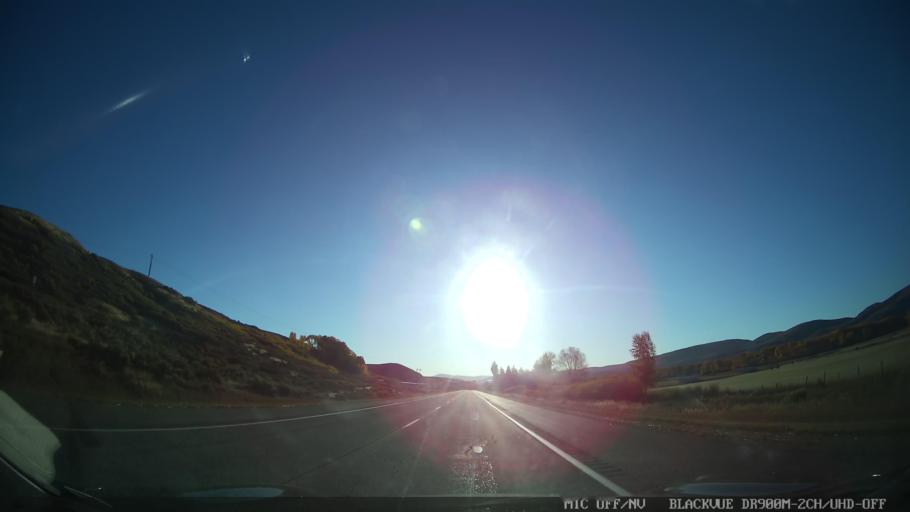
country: US
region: Colorado
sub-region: Grand County
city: Kremmling
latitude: 40.0675
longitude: -106.2652
